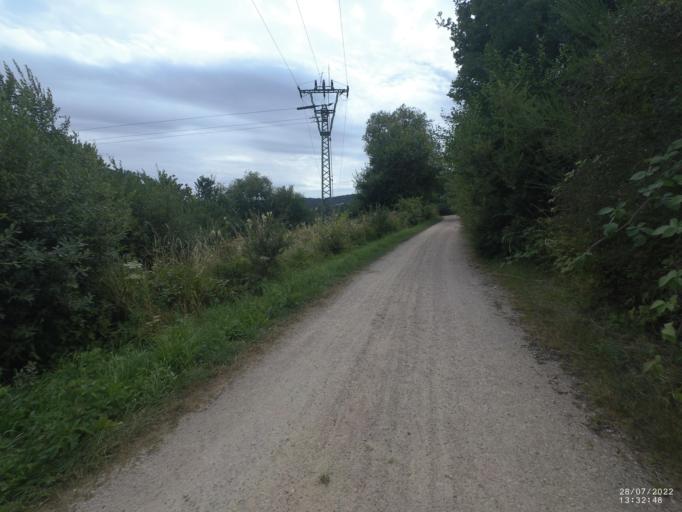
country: DE
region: Rheinland-Pfalz
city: Oberbettingen
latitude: 50.2808
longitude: 6.6344
